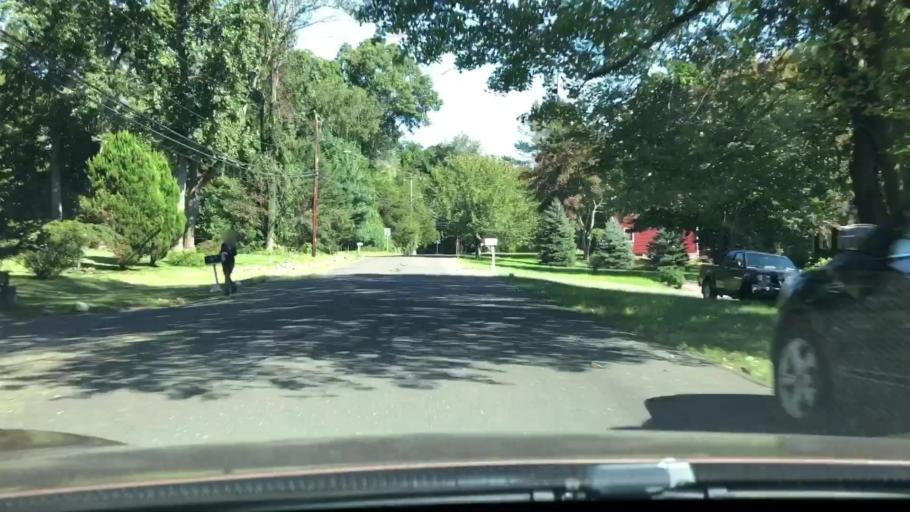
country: US
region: Connecticut
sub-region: Fairfield County
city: Darien
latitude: 41.1102
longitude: -73.4526
